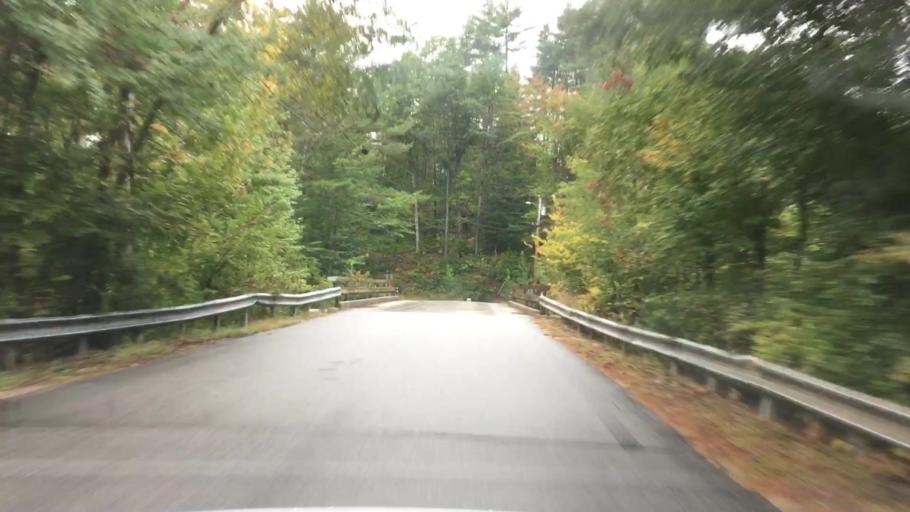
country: US
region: Maine
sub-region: Cumberland County
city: Raymond
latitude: 43.9984
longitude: -70.5718
